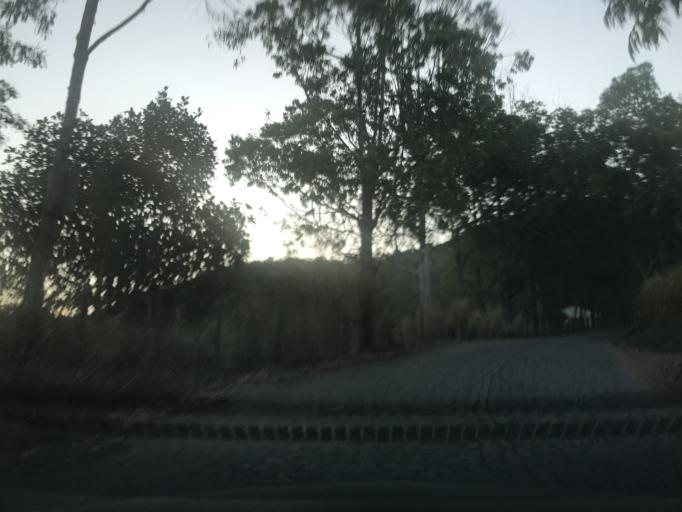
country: BR
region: Pernambuco
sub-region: Bezerros
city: Bezerros
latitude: -8.1835
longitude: -35.7676
